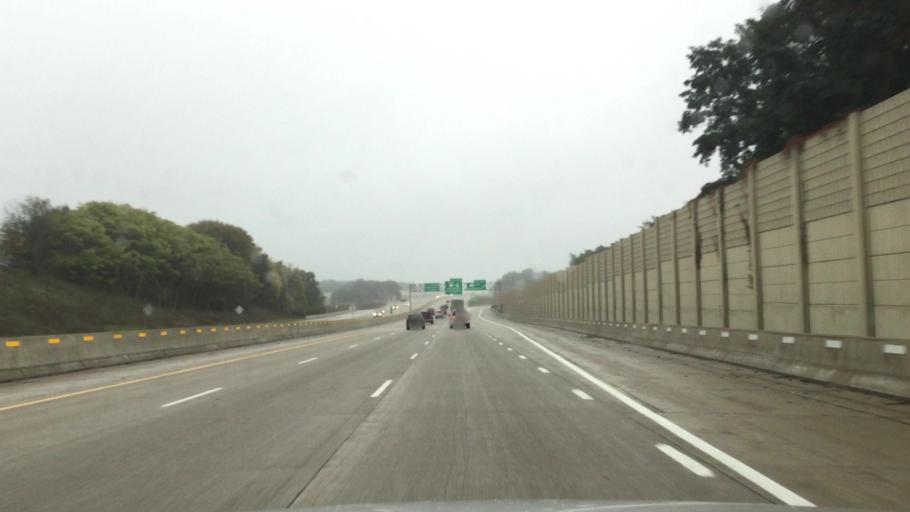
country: US
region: Michigan
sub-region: Kalamazoo County
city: Westwood
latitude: 42.2378
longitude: -85.6479
